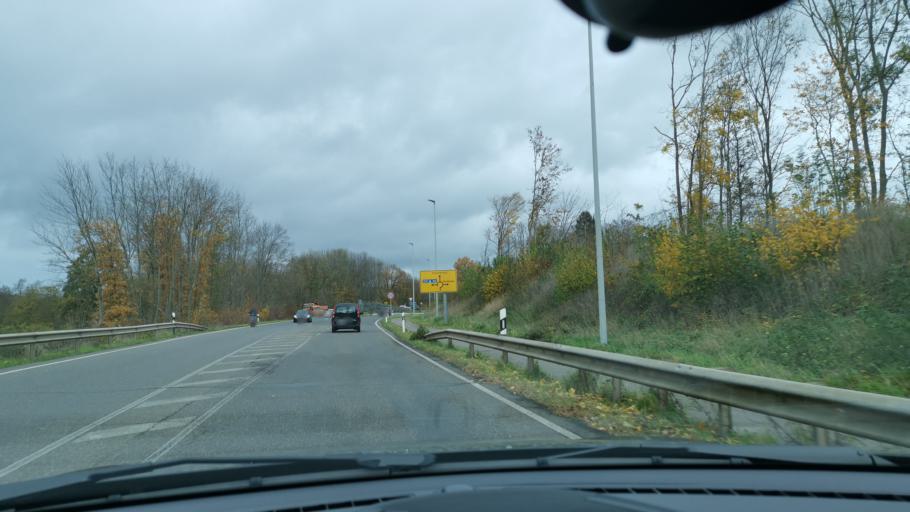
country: DE
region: North Rhine-Westphalia
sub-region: Regierungsbezirk Dusseldorf
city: Grevenbroich
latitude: 51.0738
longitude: 6.5888
